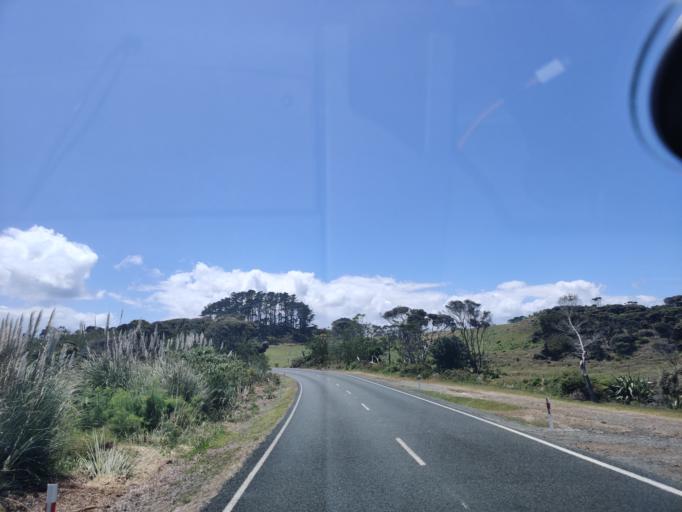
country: NZ
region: Northland
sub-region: Far North District
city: Kaitaia
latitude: -35.0328
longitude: 173.1837
